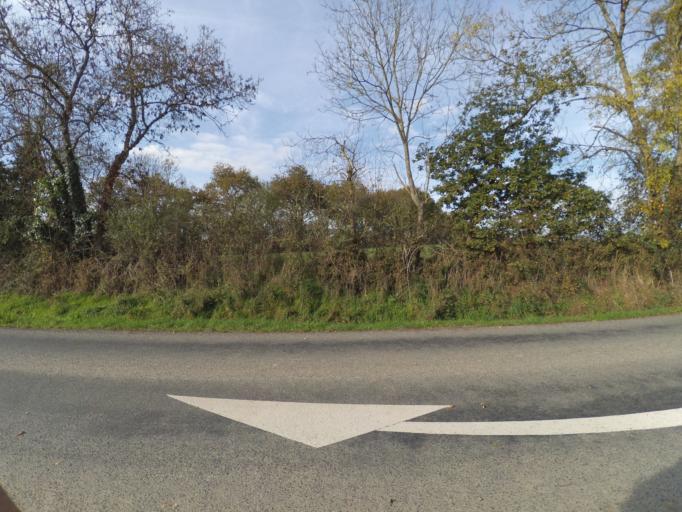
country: FR
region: Pays de la Loire
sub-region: Departement de la Vendee
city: Saint-Hilaire-de-Loulay
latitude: 47.0123
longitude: -1.3530
